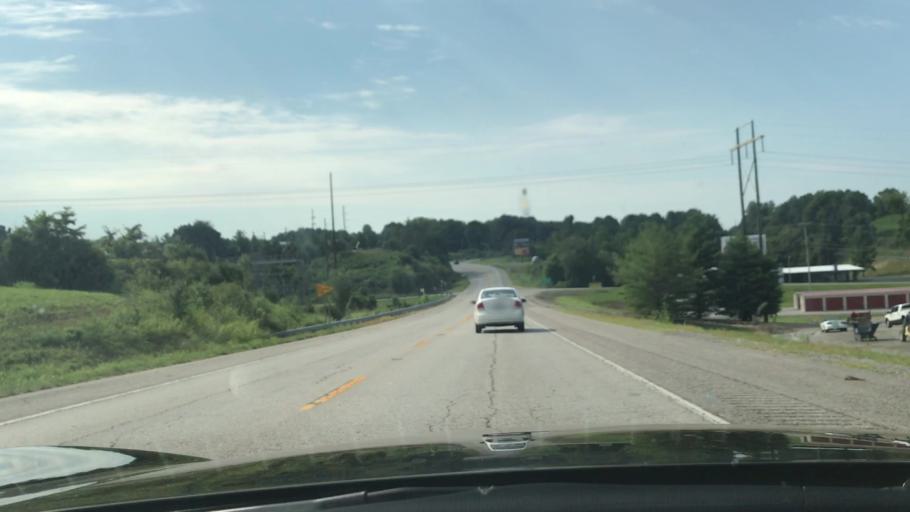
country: US
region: Kentucky
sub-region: Green County
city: Greensburg
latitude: 37.2778
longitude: -85.5121
